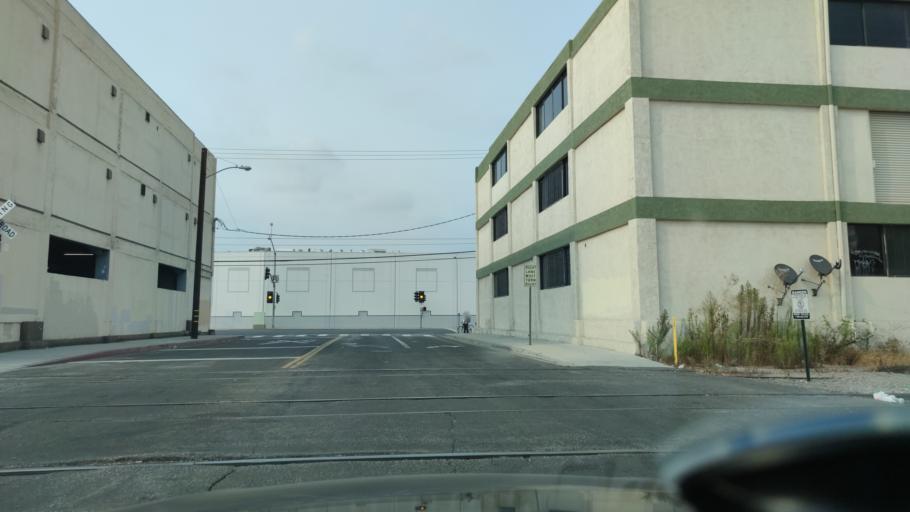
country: US
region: California
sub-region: Los Angeles County
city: Maywood
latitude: 33.9991
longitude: -118.1971
